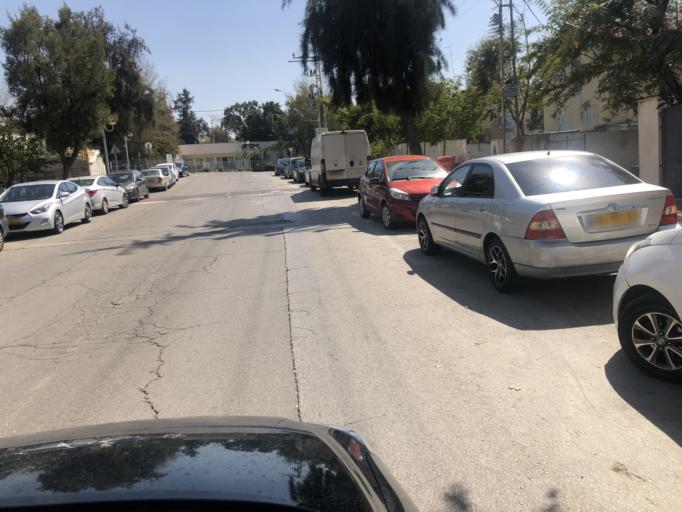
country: IL
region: Tel Aviv
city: Holon
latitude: 32.0049
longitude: 34.7632
